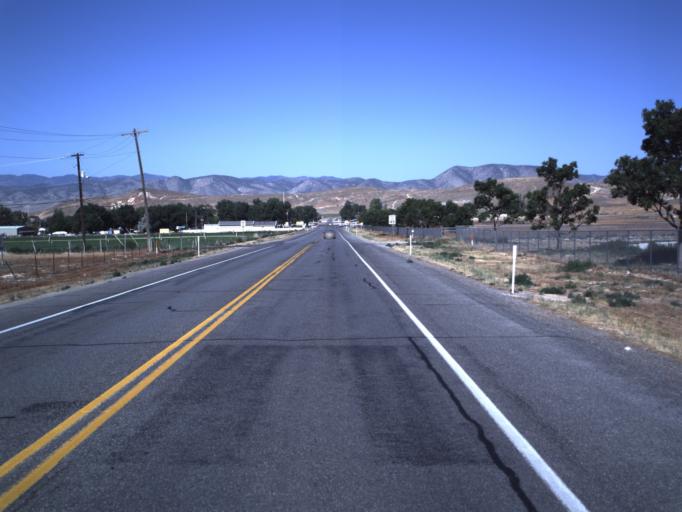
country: US
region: Utah
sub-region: Sanpete County
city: Gunnison
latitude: 39.1600
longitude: -111.8107
